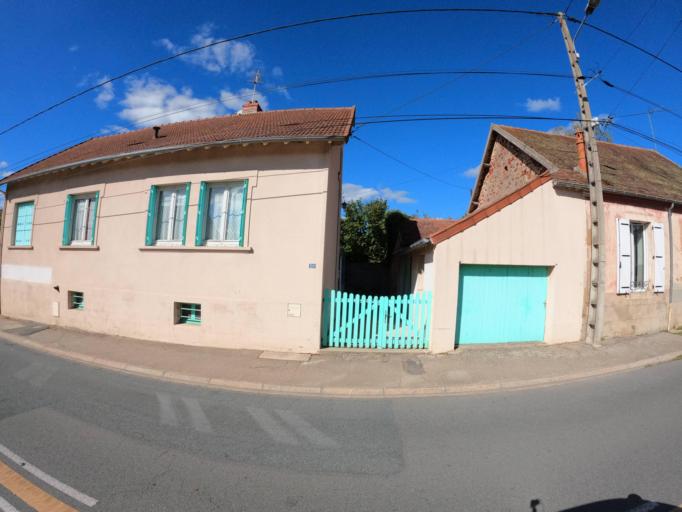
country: FR
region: Auvergne
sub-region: Departement de l'Allier
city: Doyet
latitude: 46.3970
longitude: 2.8538
